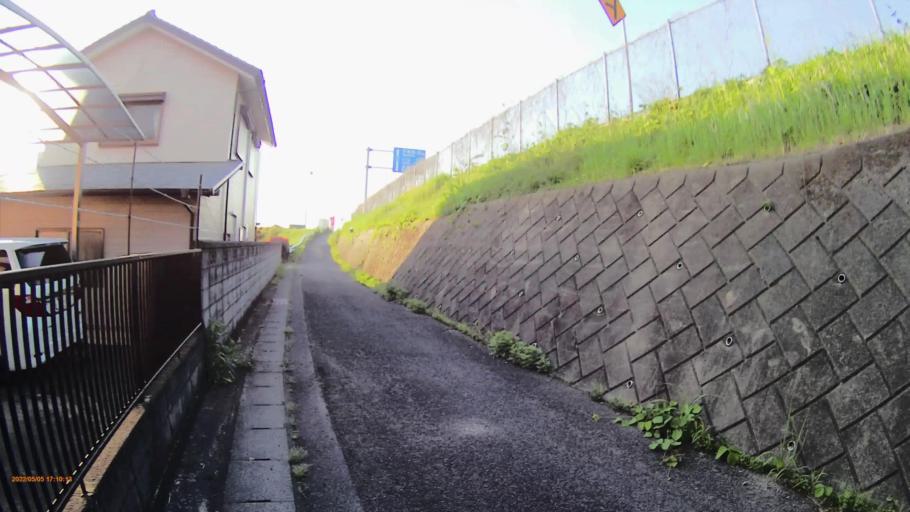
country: JP
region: Saitama
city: Kurihashi
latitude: 36.1251
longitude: 139.7126
